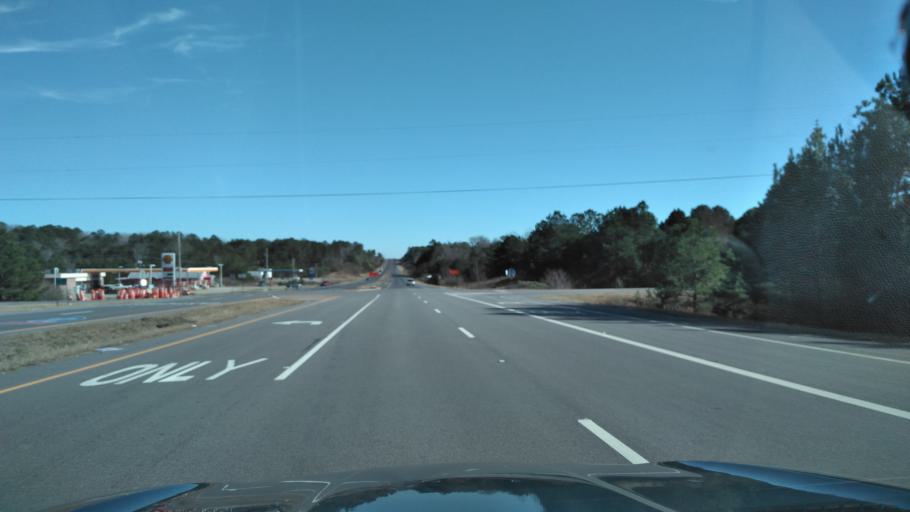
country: US
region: Alabama
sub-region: Walker County
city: Jasper
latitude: 33.8550
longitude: -87.3384
